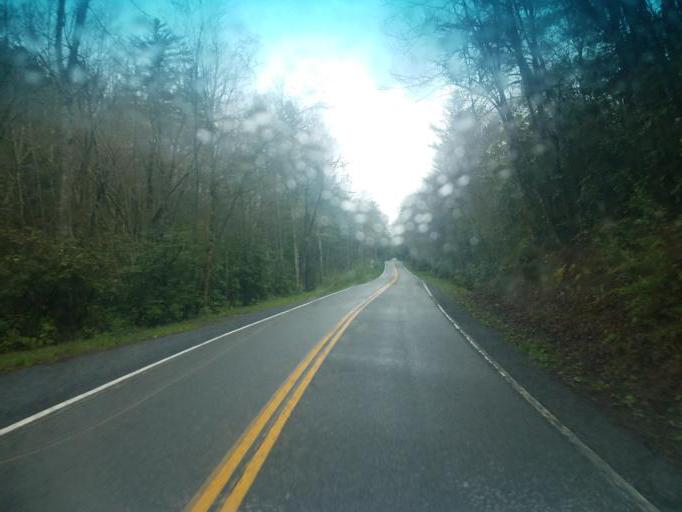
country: US
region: Virginia
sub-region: Smyth County
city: Chilhowie
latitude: 36.6529
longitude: -81.6999
